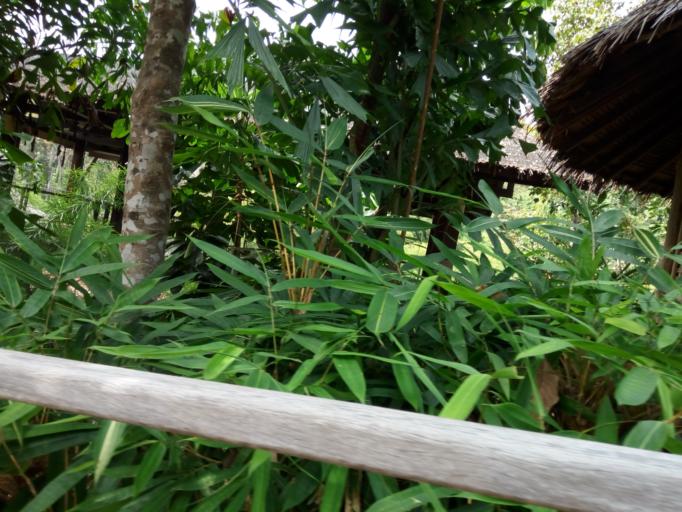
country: TH
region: Phangnga
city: Ko Yao
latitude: 8.1203
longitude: 98.6239
